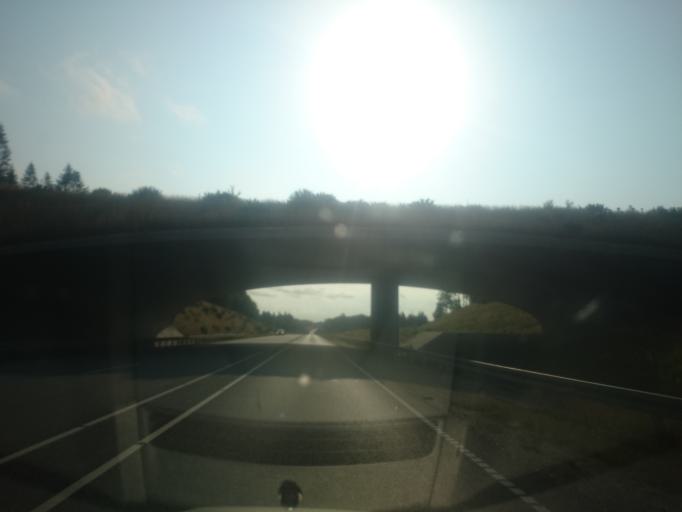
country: DK
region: South Denmark
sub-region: Vejle Kommune
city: Egtved
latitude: 55.7064
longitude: 9.2558
